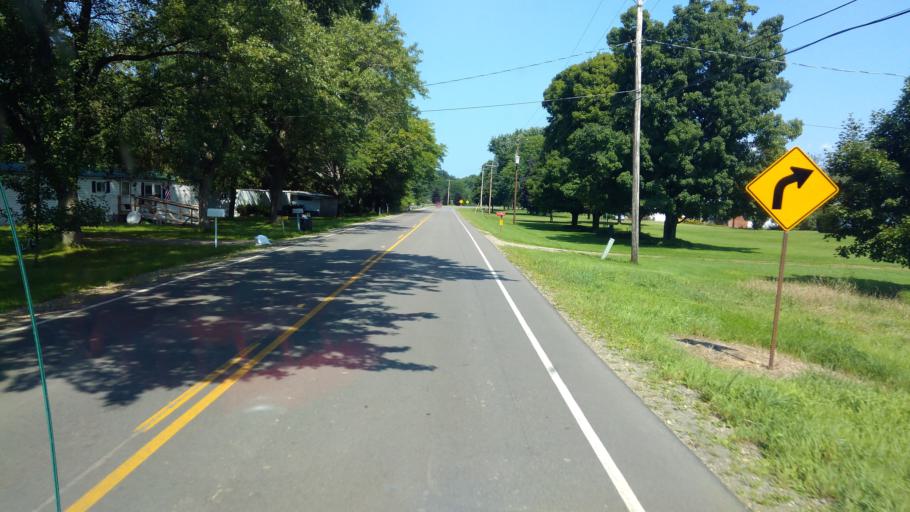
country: US
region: New York
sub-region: Allegany County
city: Belmont
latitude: 42.2359
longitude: -78.0391
